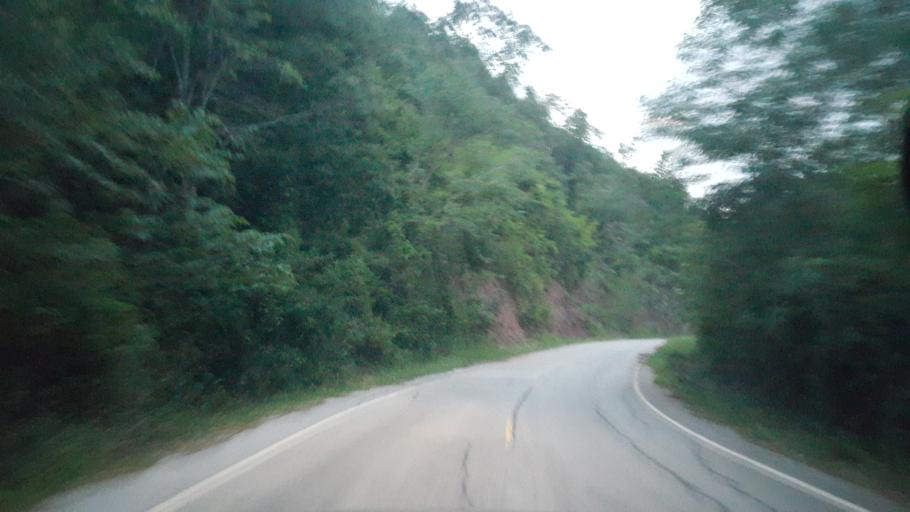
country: TH
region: Loei
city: Phu Ruea
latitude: 17.5263
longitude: 101.2290
